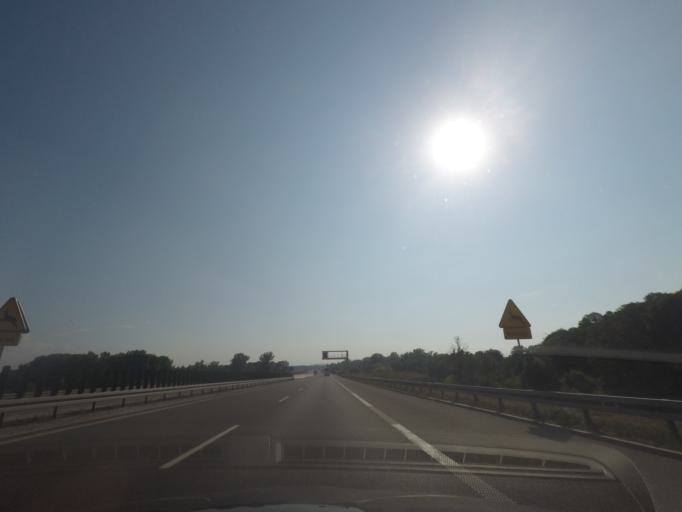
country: PL
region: Silesian Voivodeship
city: Gorzyczki
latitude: 49.9369
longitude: 18.4081
